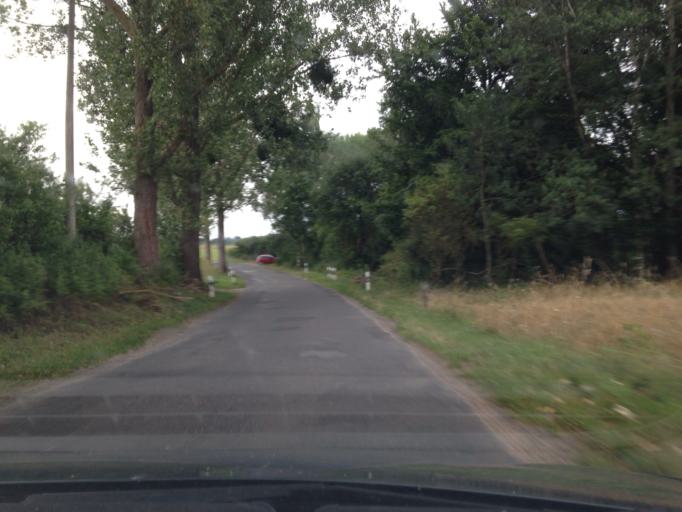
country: DE
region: Mecklenburg-Vorpommern
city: Loitz
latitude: 53.3148
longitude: 13.4190
